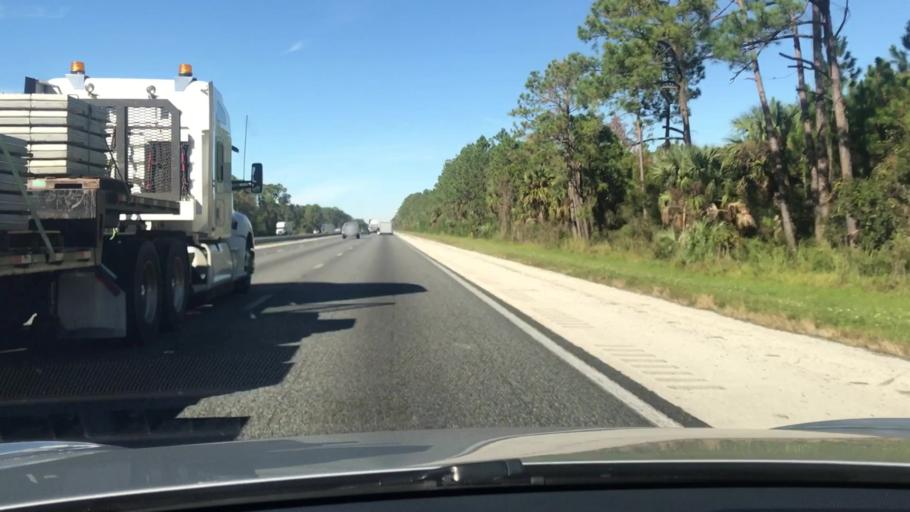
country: US
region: Florida
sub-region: Volusia County
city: Ormond-by-the-Sea
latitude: 29.3634
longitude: -81.1375
